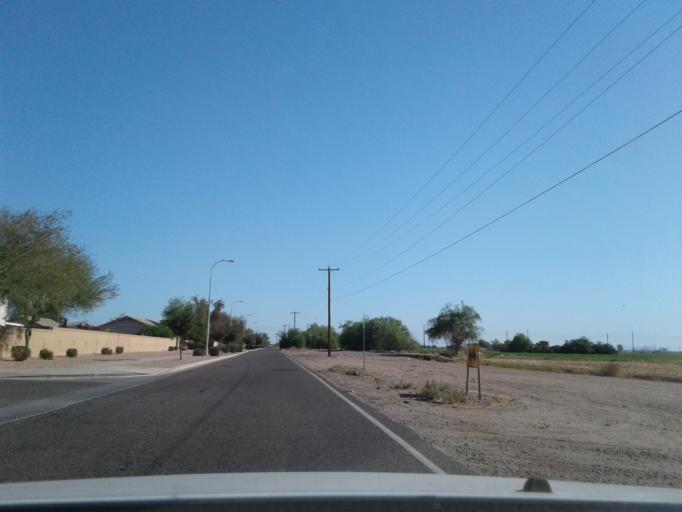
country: US
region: Arizona
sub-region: Maricopa County
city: Laveen
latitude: 33.4182
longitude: -112.1954
